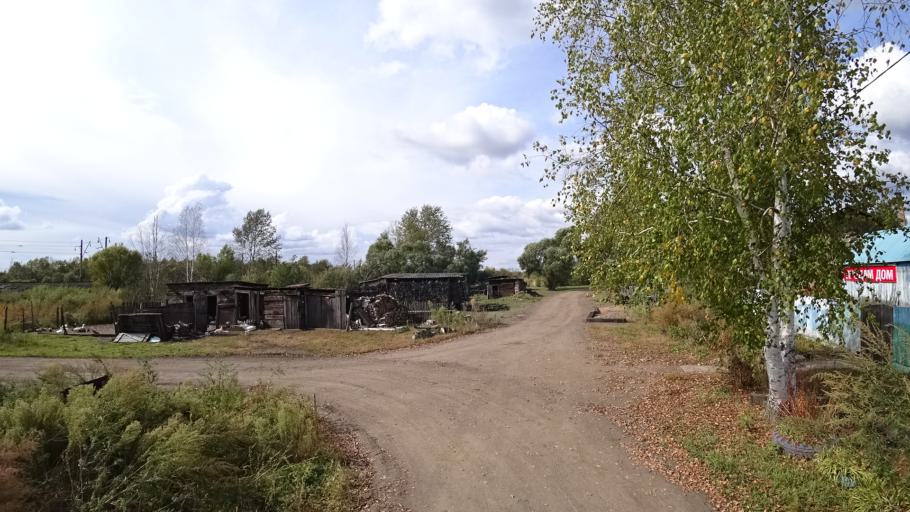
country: RU
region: Amur
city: Arkhara
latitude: 49.3535
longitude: 130.1576
